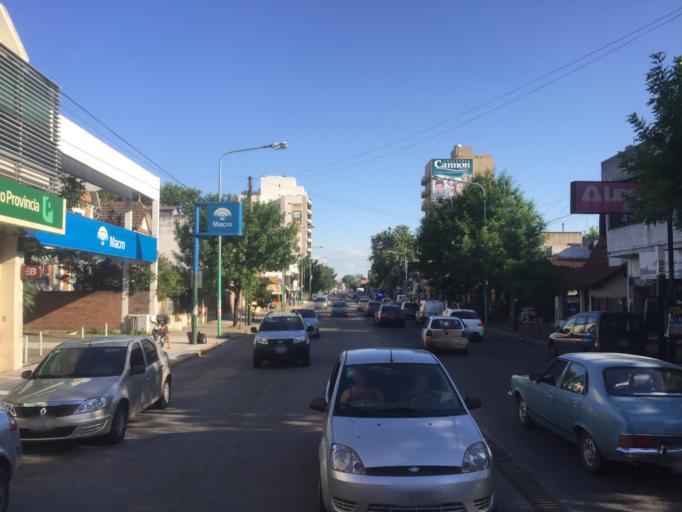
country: AR
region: Buenos Aires
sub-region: Partido de Lomas de Zamora
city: Lomas de Zamora
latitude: -34.7738
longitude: -58.3939
